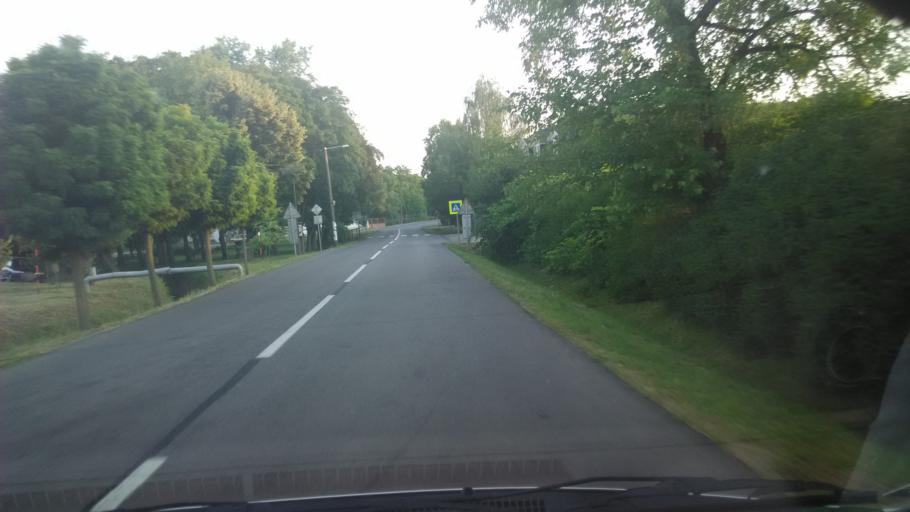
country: SK
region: Nitriansky
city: Tlmace
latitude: 48.1571
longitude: 18.4502
